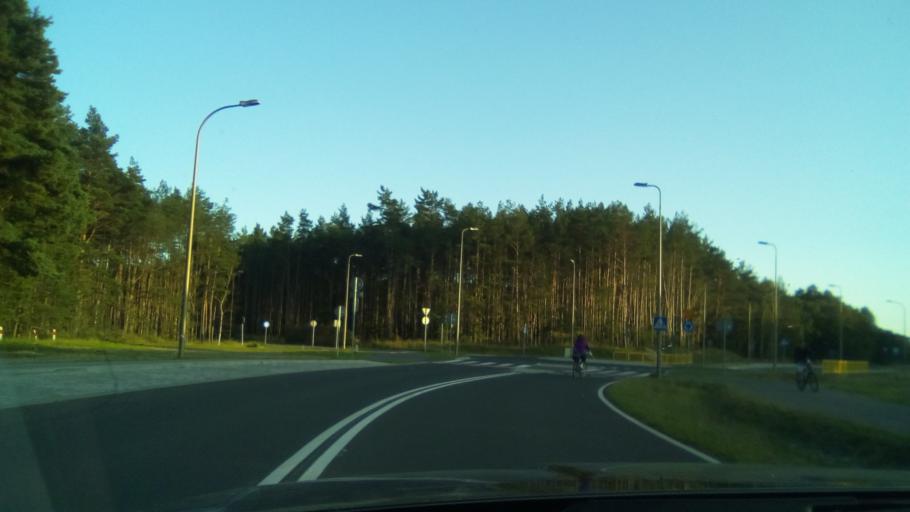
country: PL
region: West Pomeranian Voivodeship
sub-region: Swinoujscie
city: Swinoujscie
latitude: 53.9161
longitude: 14.3009
